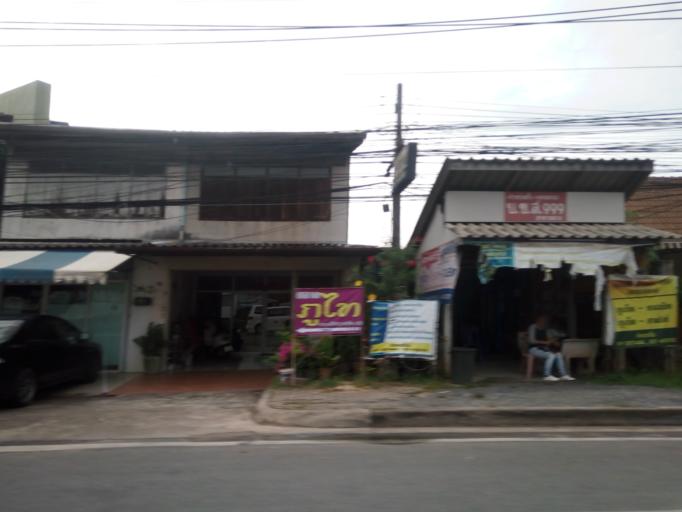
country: TH
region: Phuket
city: Thalang
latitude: 8.0338
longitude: 98.3332
